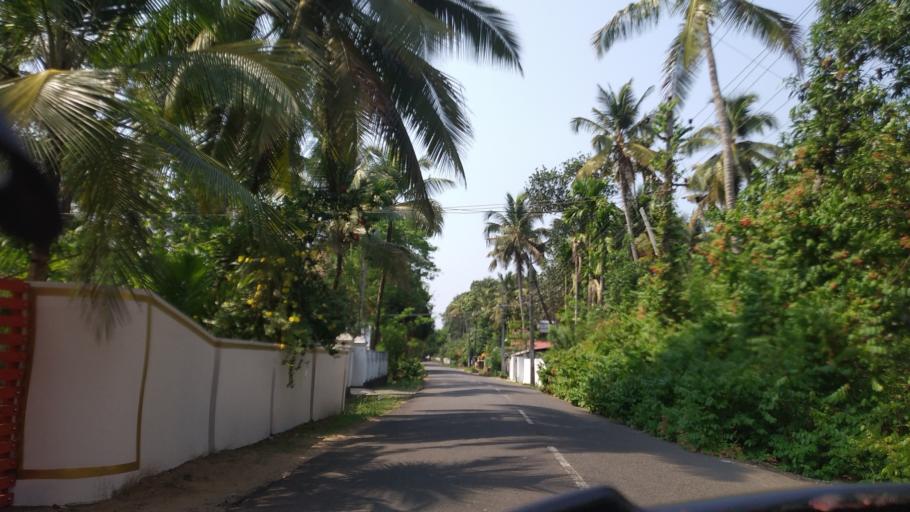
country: IN
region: Kerala
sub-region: Thrissur District
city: Irinjalakuda
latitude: 10.3240
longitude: 76.1235
